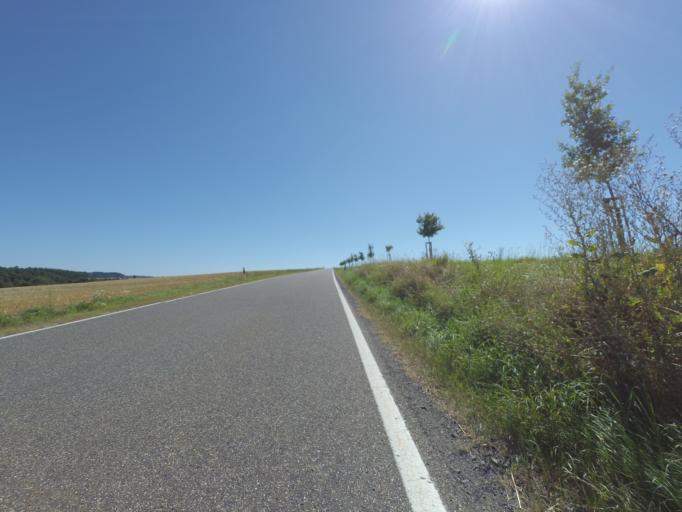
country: DE
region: Rheinland-Pfalz
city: Lutzerath
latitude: 50.1397
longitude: 7.0054
